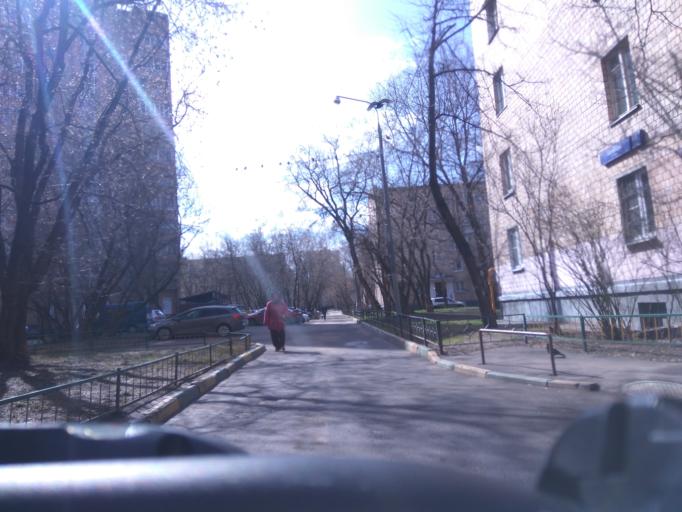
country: RU
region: Moskovskaya
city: Fili
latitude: 55.7432
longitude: 37.4897
